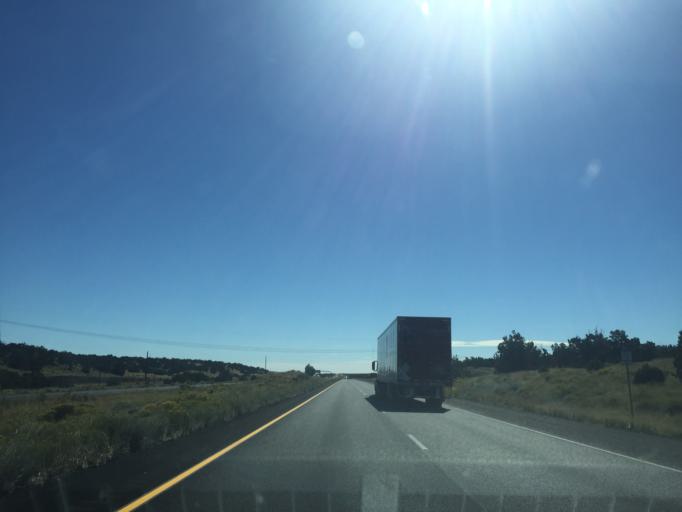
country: US
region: Arizona
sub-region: Coconino County
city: Flagstaff
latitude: 35.1983
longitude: -111.3989
